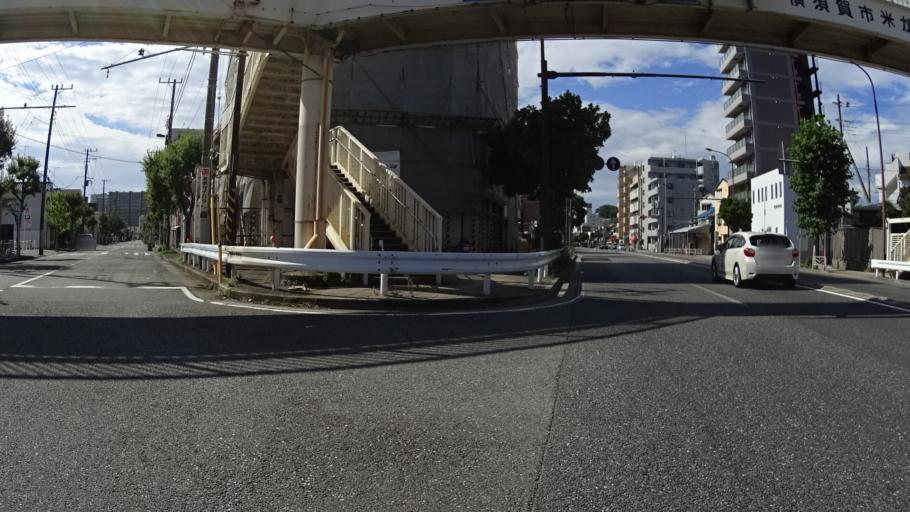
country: JP
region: Kanagawa
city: Yokosuka
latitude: 35.2758
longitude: 139.6771
